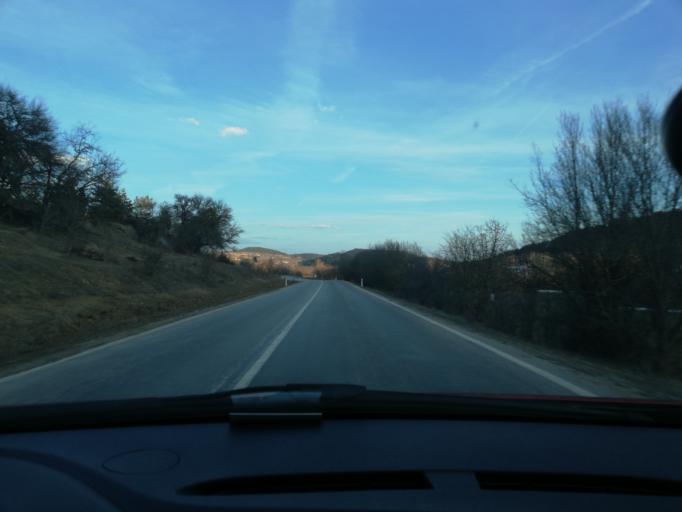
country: TR
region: Kastamonu
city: Agli
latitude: 41.6920
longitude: 33.5880
